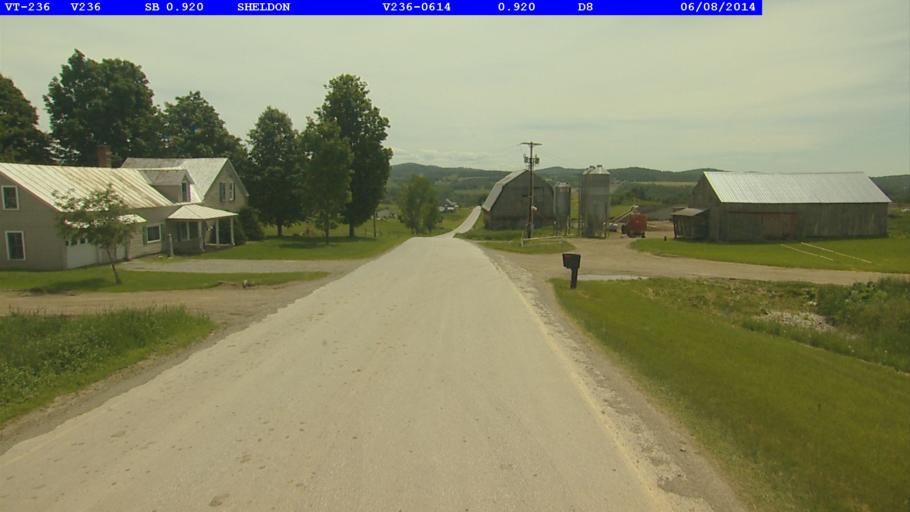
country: US
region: Vermont
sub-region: Franklin County
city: Enosburg Falls
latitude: 44.9241
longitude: -72.8656
